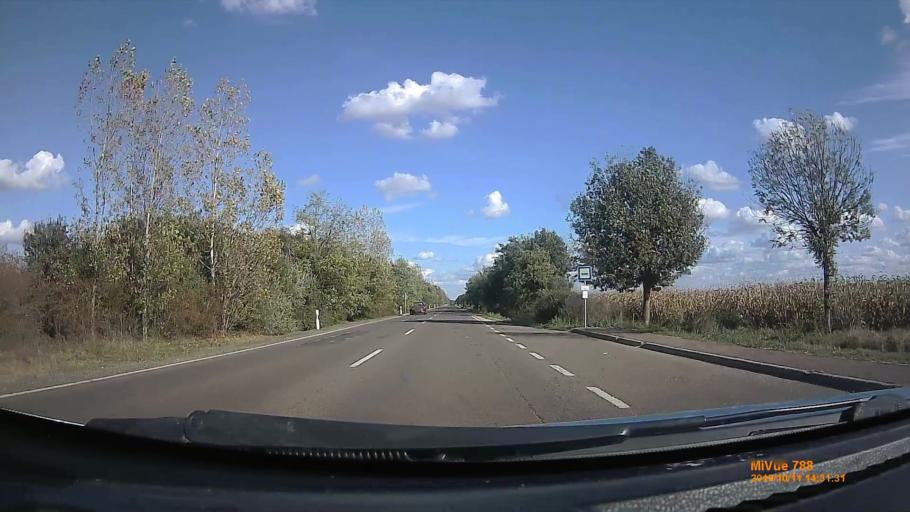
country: HU
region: Hajdu-Bihar
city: Balmazujvaros
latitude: 47.5616
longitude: 21.4206
